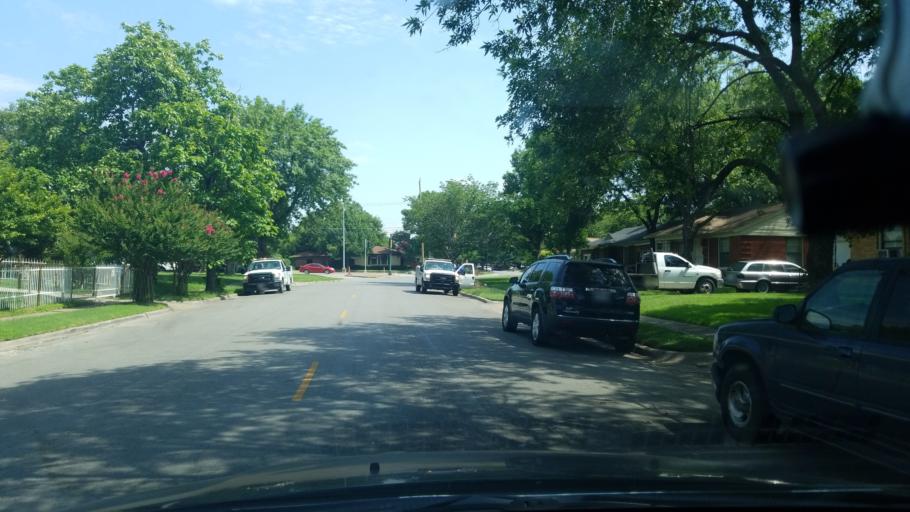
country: US
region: Texas
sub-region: Dallas County
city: Balch Springs
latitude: 32.7480
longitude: -96.6920
